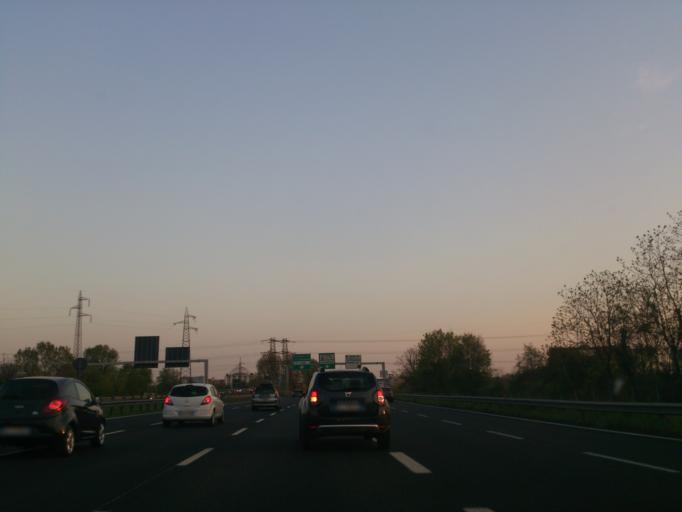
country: IT
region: Lombardy
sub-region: Citta metropolitana di Milano
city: Cologno Monzese
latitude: 45.5182
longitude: 9.2614
